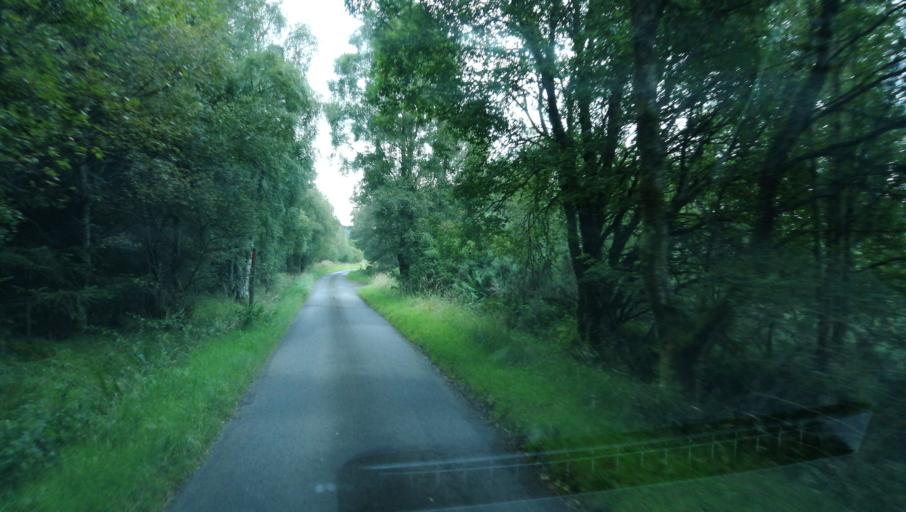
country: GB
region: Scotland
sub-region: Perth and Kinross
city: Blairgowrie
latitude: 56.6596
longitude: -3.3133
